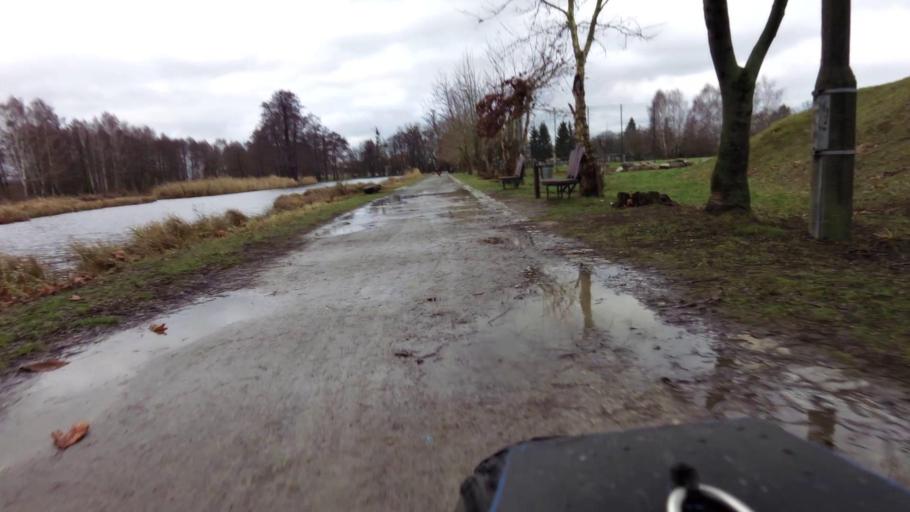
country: PL
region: Lubusz
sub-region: Powiat gorzowski
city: Witnica
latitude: 52.6779
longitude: 14.8951
